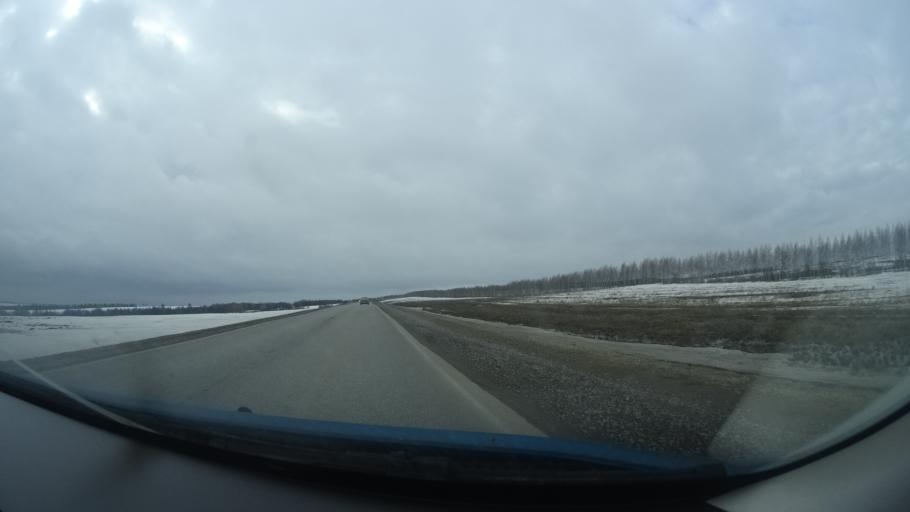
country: RU
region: Bashkortostan
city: Birsk
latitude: 55.3835
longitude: 55.5808
